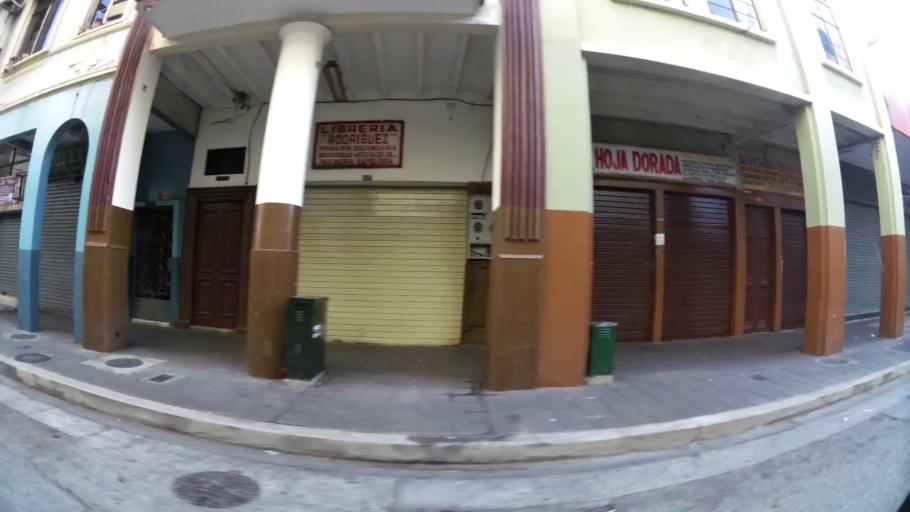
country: EC
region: Guayas
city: Guayaquil
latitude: -2.1938
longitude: -79.8854
